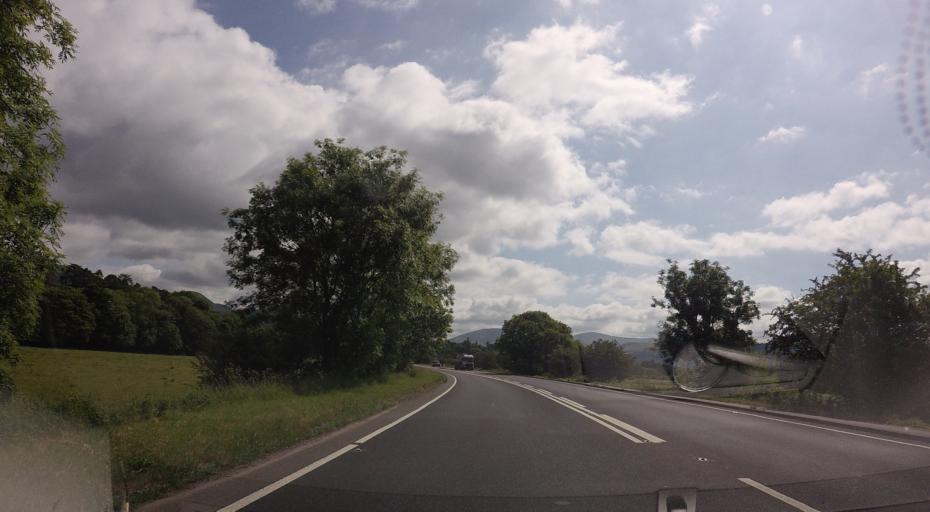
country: GB
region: England
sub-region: Cumbria
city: Keswick
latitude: 54.6008
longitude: -3.1747
